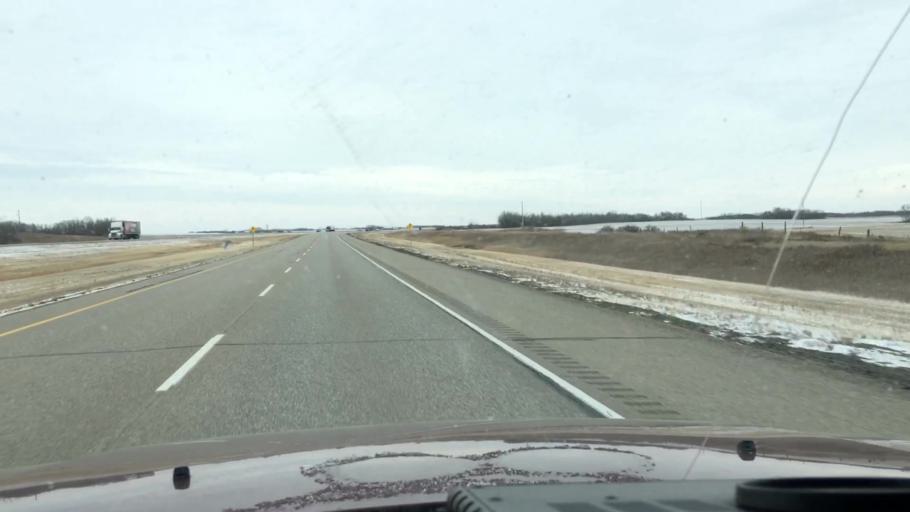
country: CA
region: Saskatchewan
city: Watrous
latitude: 51.3368
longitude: -106.0903
